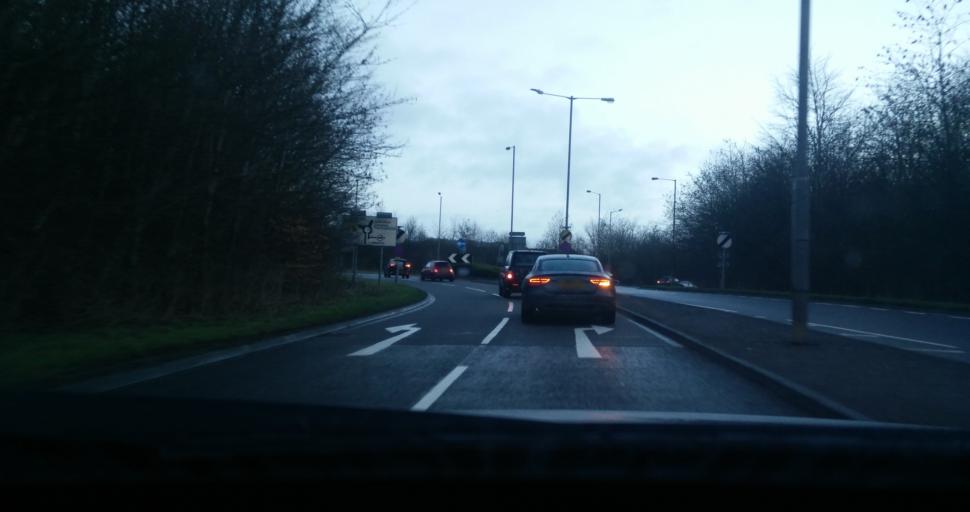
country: GB
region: England
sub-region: Buckinghamshire
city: Amersham
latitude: 51.6607
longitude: -0.6240
